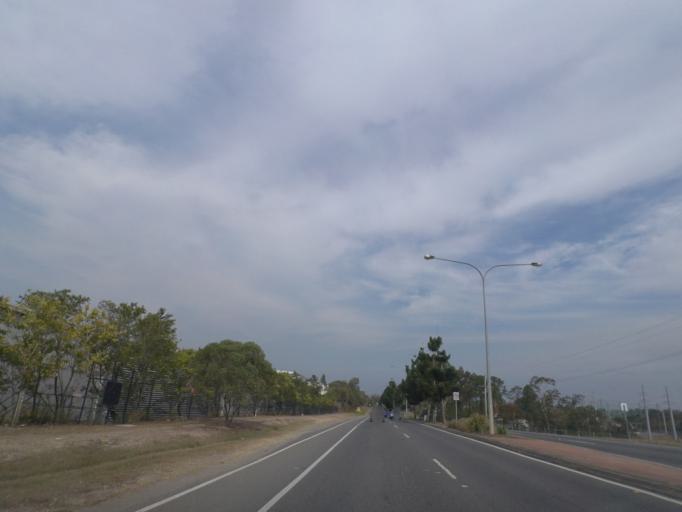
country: AU
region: Queensland
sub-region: Brisbane
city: Sunnybank
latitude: -27.5974
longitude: 153.0288
